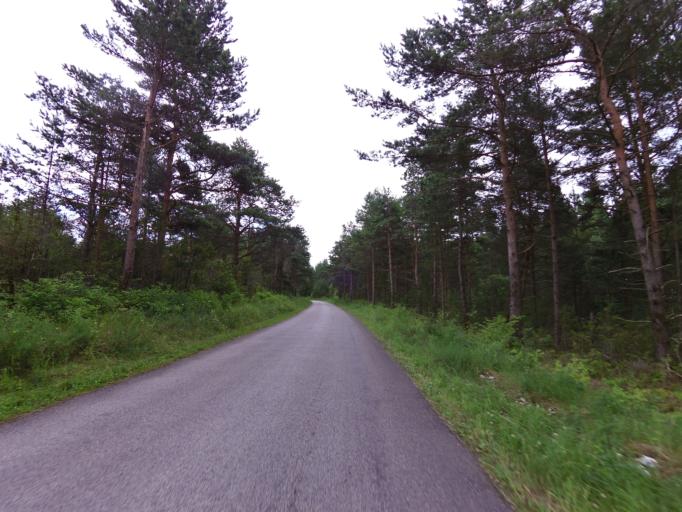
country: EE
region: Laeaene
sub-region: Vormsi vald
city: Hullo
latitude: 58.9818
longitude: 23.2498
